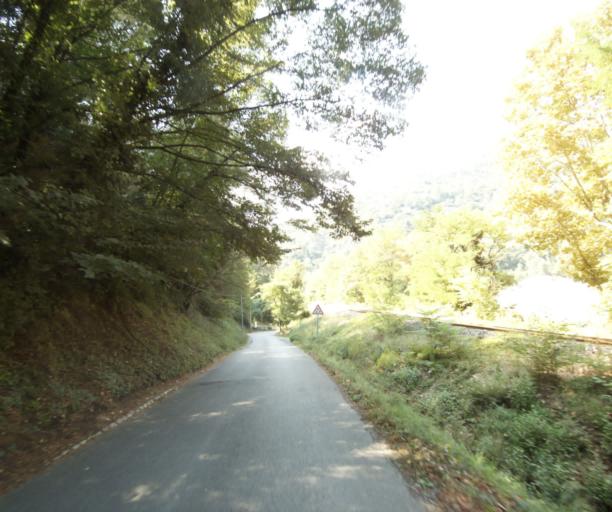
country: FR
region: Provence-Alpes-Cote d'Azur
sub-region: Departement des Alpes-Maritimes
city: Cantaron
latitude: 43.7641
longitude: 7.3257
